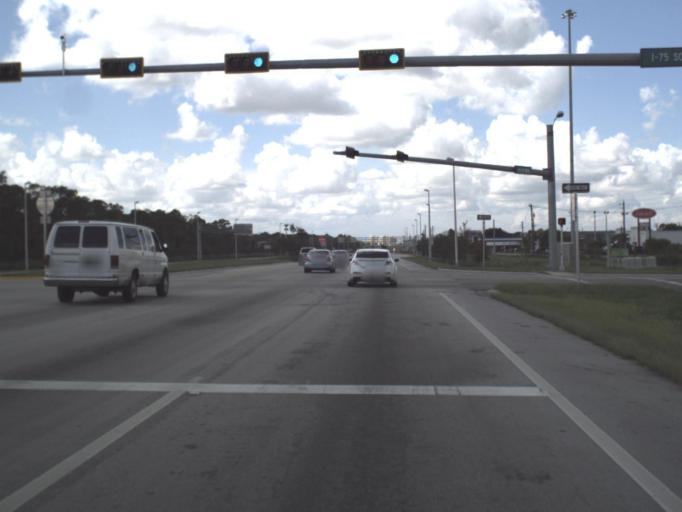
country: US
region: Florida
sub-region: Lee County
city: Fort Myers
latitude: 26.6354
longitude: -81.8038
